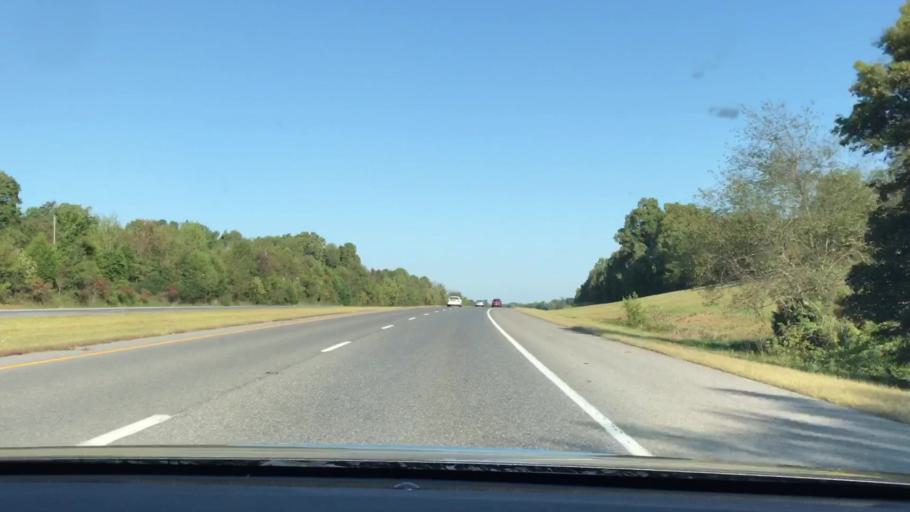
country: US
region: Kentucky
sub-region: Marshall County
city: Benton
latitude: 36.7780
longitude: -88.3213
